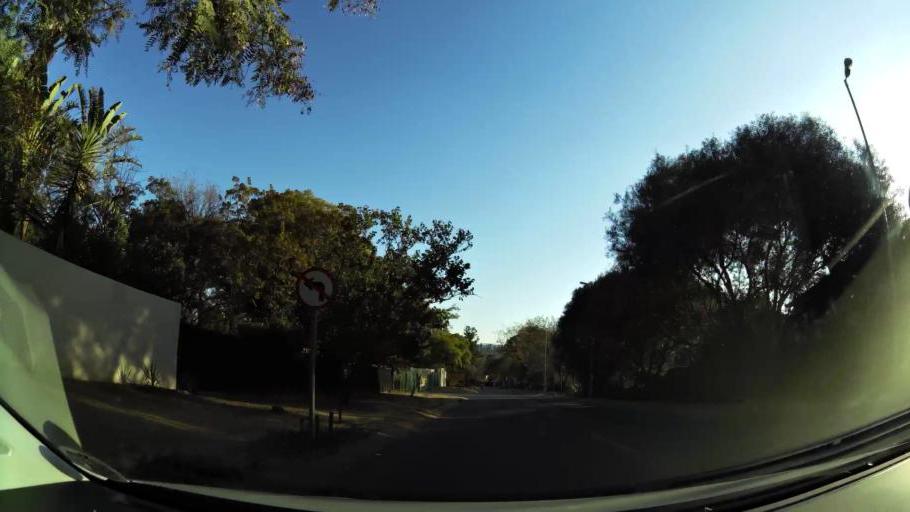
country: ZA
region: Gauteng
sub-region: City of Johannesburg Metropolitan Municipality
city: Modderfontein
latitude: -26.0730
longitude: 28.0770
